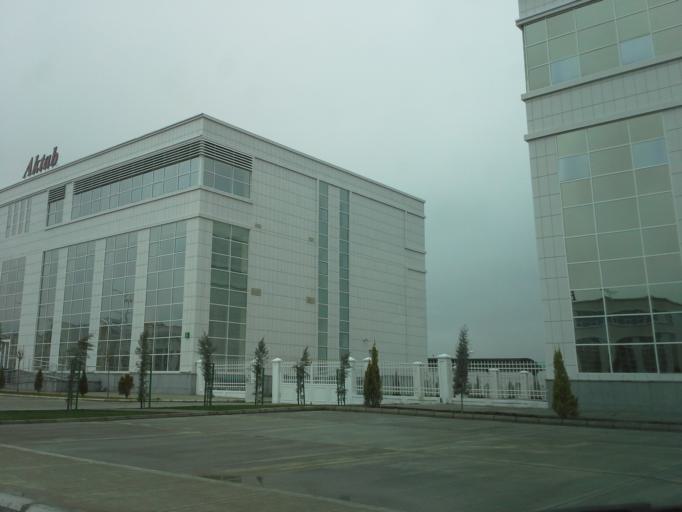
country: TM
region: Ahal
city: Ashgabat
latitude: 37.9683
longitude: 58.4077
